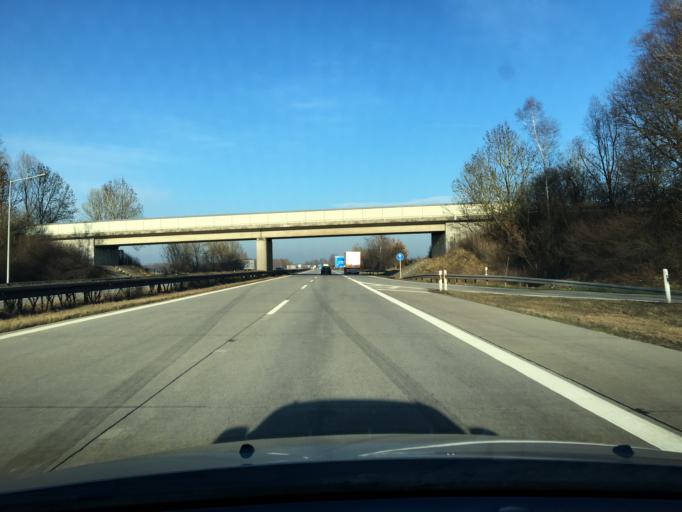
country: DE
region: Bavaria
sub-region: Upper Bavaria
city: Langenpreising
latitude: 48.4388
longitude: 11.9541
